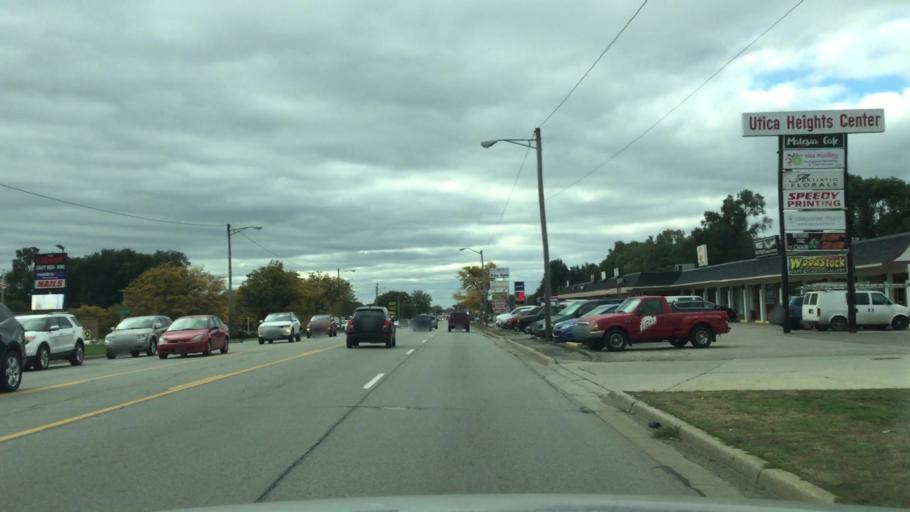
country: US
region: Michigan
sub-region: Macomb County
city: Utica
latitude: 42.6392
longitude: -83.0329
